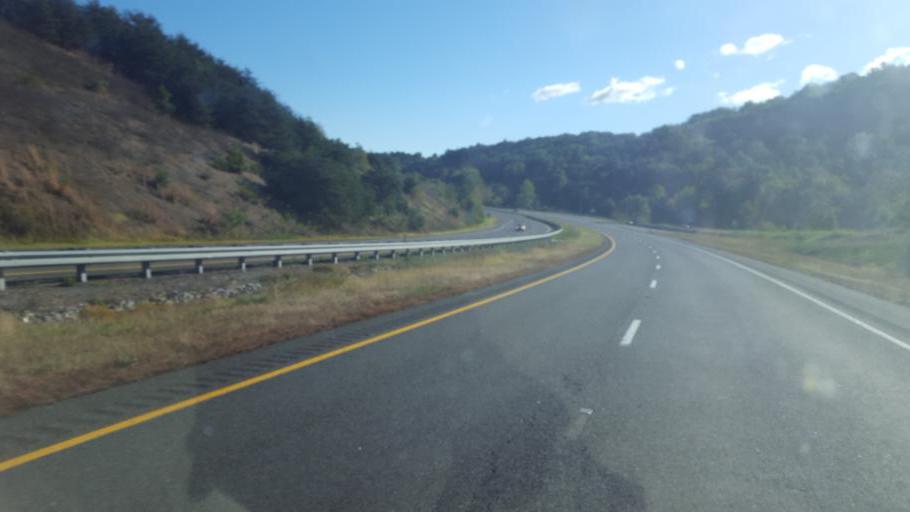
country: US
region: Maryland
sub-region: Washington County
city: Hancock
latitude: 39.6979
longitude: -78.2462
